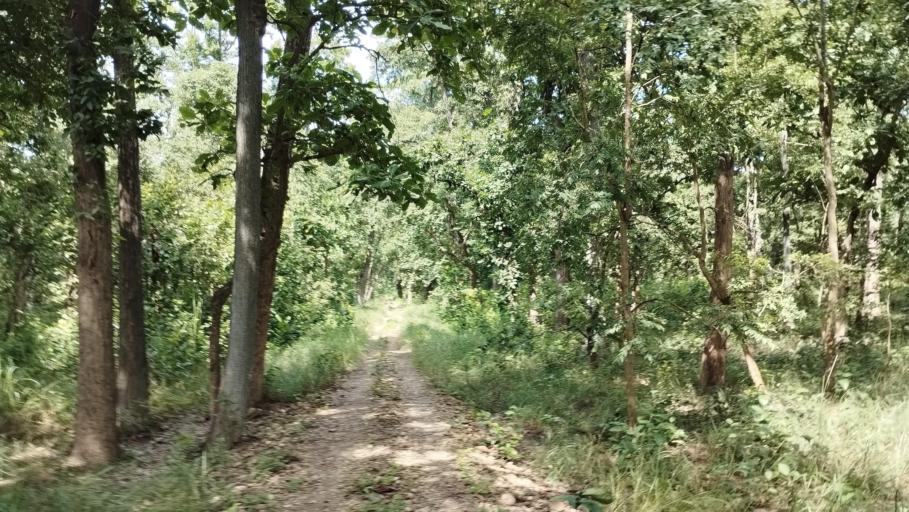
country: NP
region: Far Western
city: Tikapur
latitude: 28.5166
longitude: 81.2738
